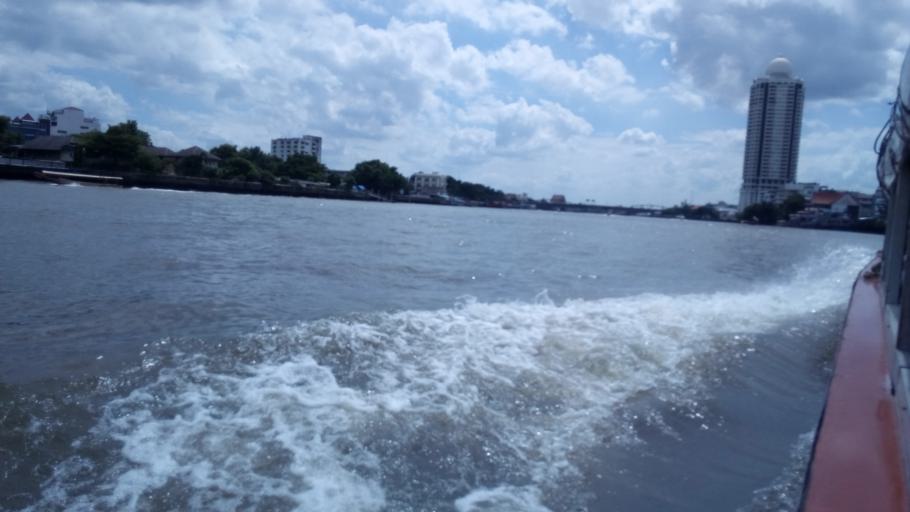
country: TH
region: Bangkok
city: Khlong San
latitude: 13.7368
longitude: 100.5076
